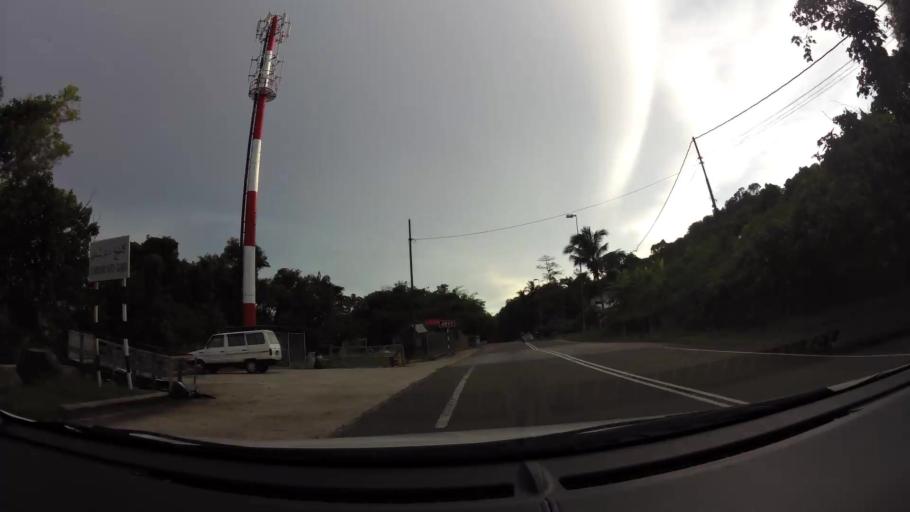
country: BN
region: Brunei and Muara
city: Bandar Seri Begawan
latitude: 4.8966
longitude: 114.9850
